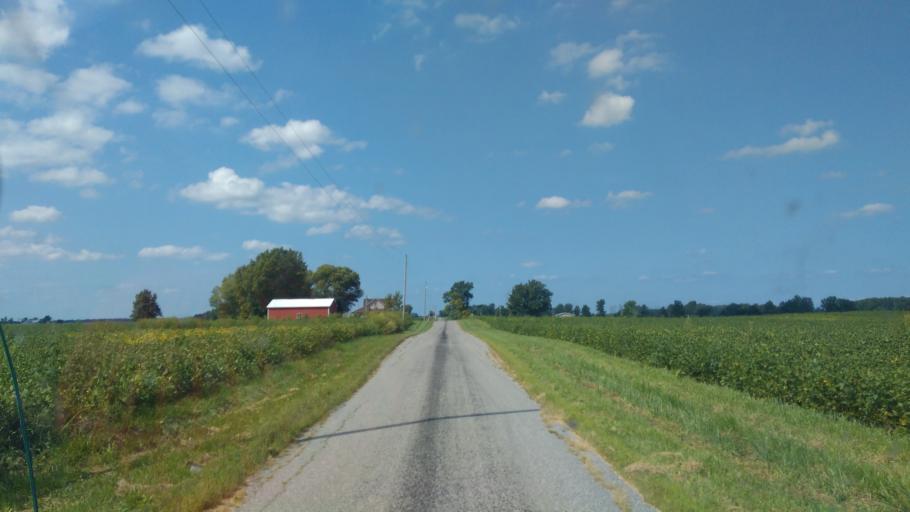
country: US
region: Ohio
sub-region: Union County
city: Richwood
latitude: 40.5006
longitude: -83.4495
